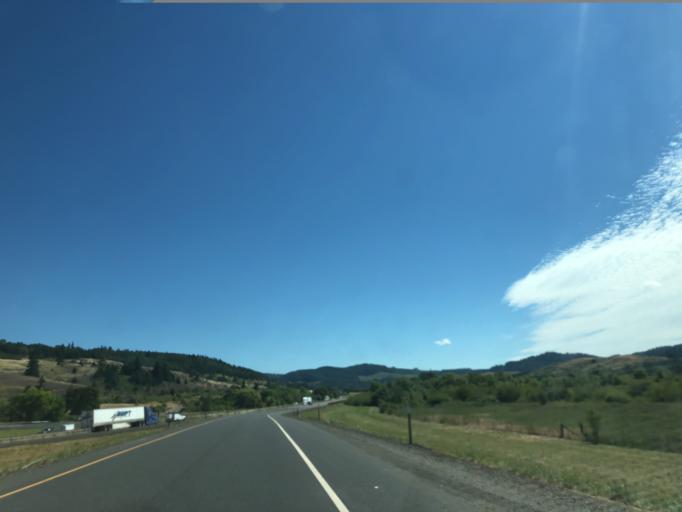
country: US
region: Oregon
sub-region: Douglas County
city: Yoncalla
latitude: 43.5639
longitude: -123.2811
